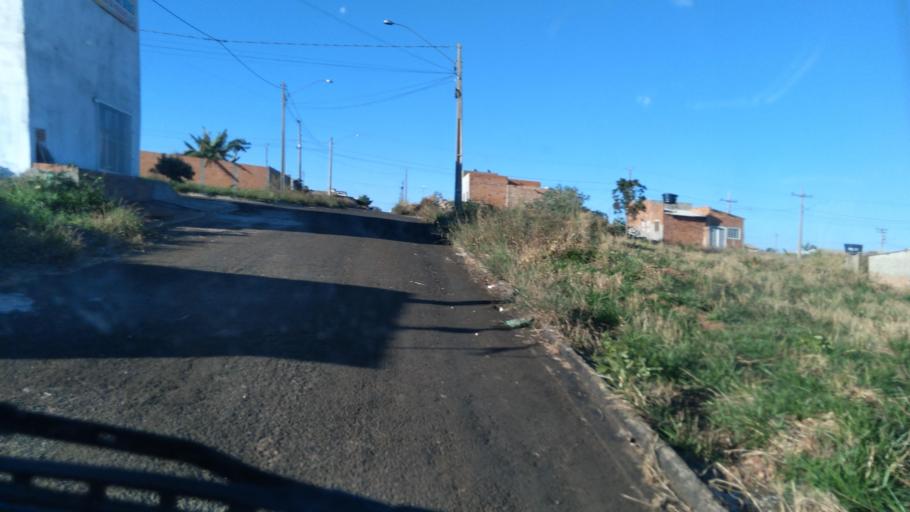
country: BR
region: Goias
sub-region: Mineiros
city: Mineiros
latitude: -17.5429
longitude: -52.5566
